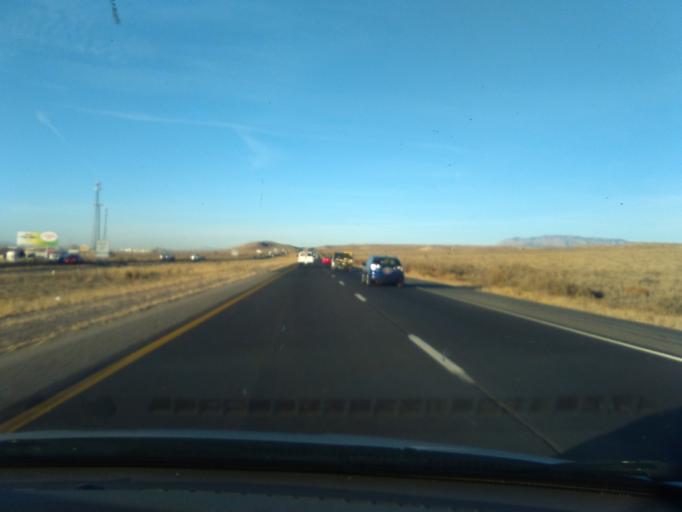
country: US
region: New Mexico
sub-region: Bernalillo County
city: South Valley
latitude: 34.9646
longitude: -106.6566
